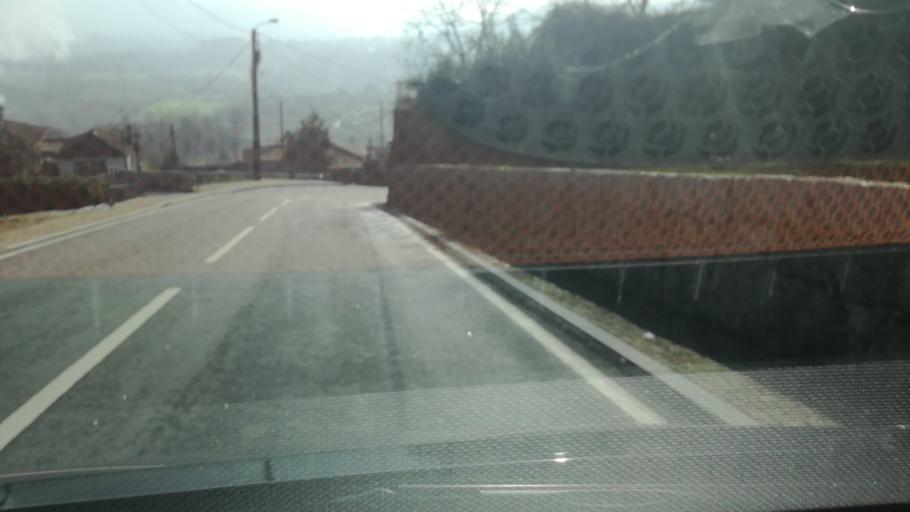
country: PT
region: Braga
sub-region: Guimaraes
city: Ponte
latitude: 41.5274
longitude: -8.3404
